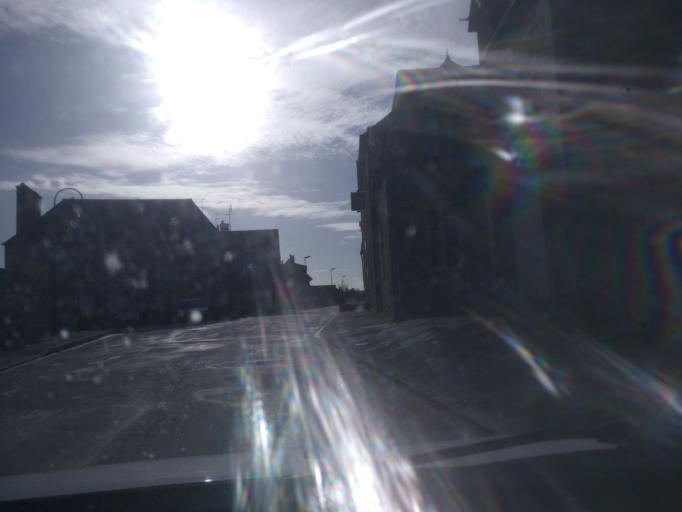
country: FR
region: Brittany
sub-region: Departement d'Ille-et-Vilaine
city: Antrain
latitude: 48.4602
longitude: -1.4858
